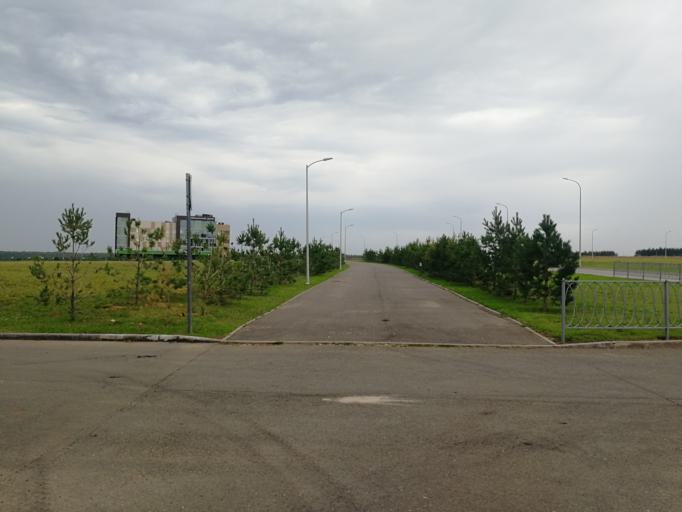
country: RU
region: Tatarstan
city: Sviyazhsk
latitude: 55.7542
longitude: 48.7454
